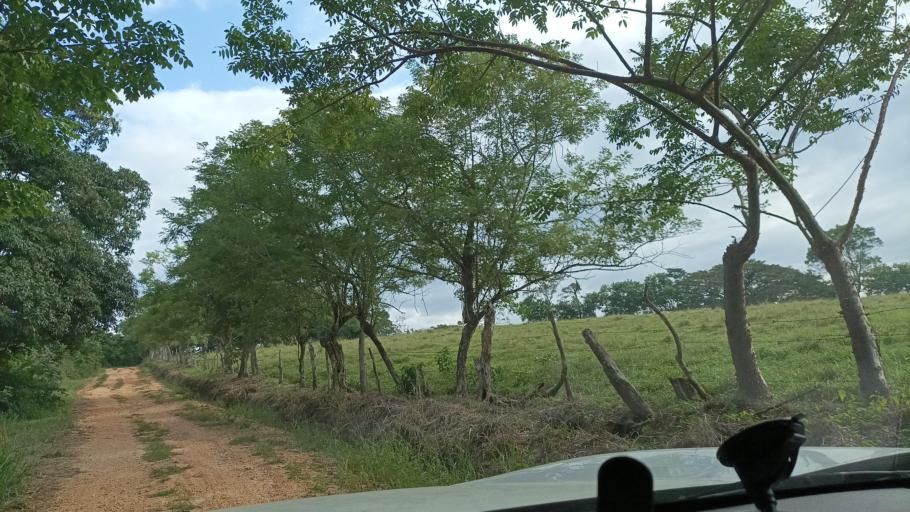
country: MX
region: Veracruz
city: Soconusco
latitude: 17.9445
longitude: -94.8827
